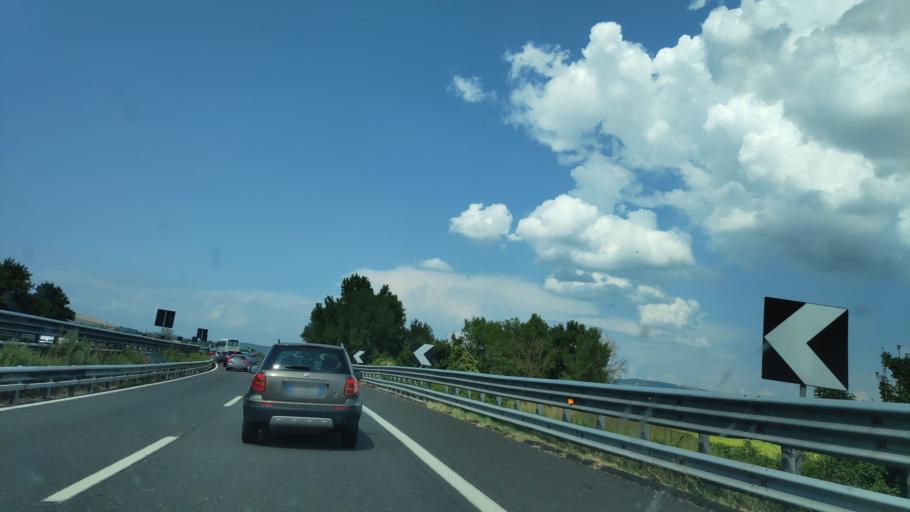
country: IT
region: Umbria
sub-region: Provincia di Terni
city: Fabro Scalo
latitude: 42.8602
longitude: 12.0381
